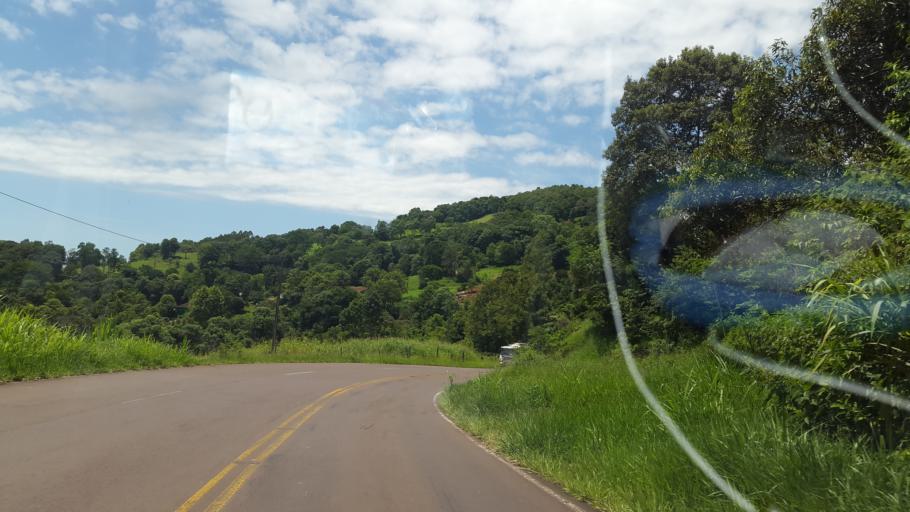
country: BR
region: Rio Grande do Sul
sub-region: Frederico Westphalen
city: Frederico Westphalen
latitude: -27.0642
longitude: -53.4743
